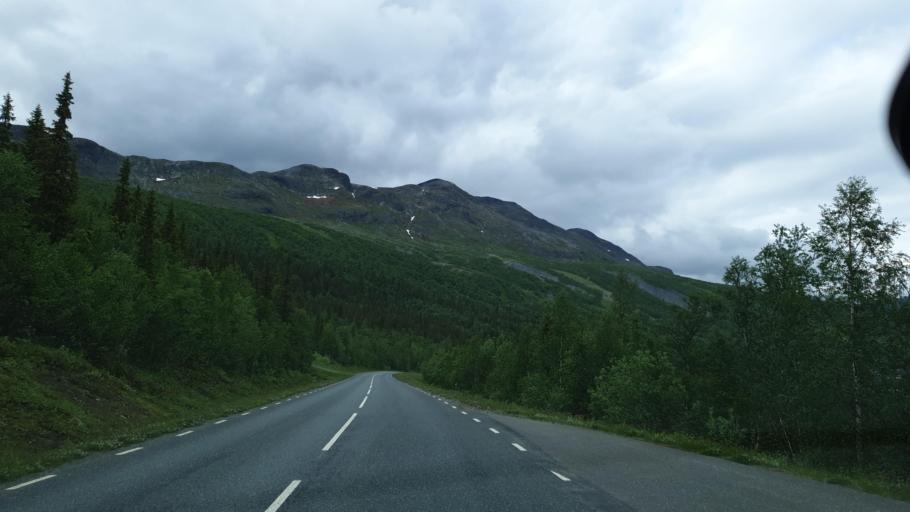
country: SE
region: Vaesterbotten
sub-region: Vilhelmina Kommun
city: Sjoberg
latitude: 65.2417
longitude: 15.4744
